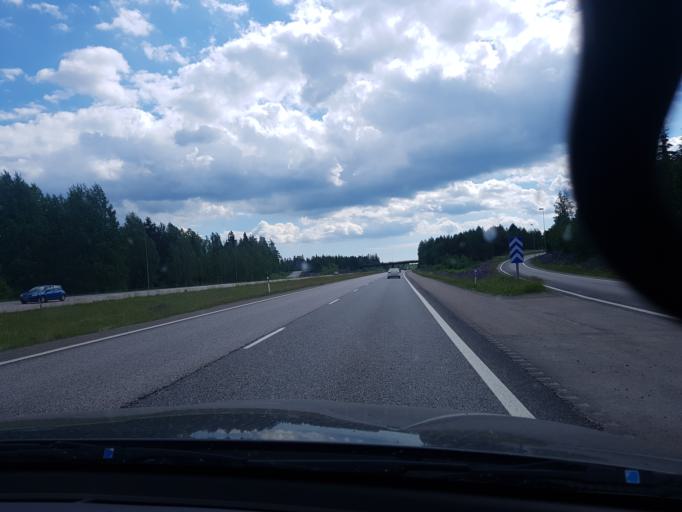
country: FI
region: Uusimaa
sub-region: Helsinki
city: Nurmijaervi
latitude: 60.4602
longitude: 24.8479
